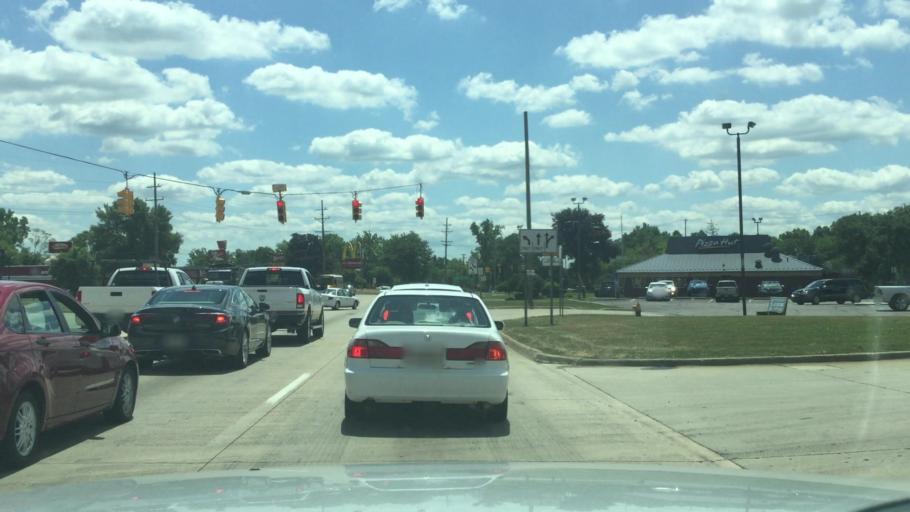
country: US
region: Michigan
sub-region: Wayne County
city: Belleville
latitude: 42.2157
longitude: -83.5445
